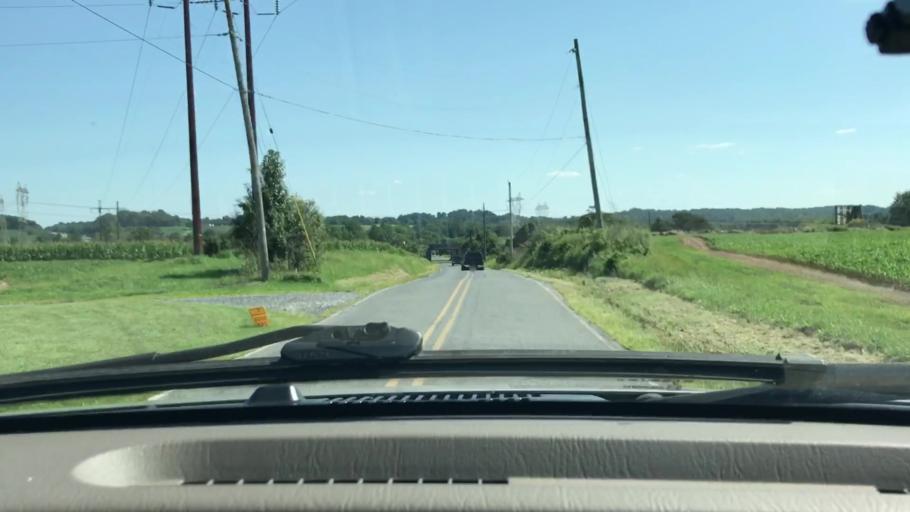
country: US
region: Pennsylvania
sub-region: Lancaster County
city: Elizabethtown
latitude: 40.1910
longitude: -76.6155
